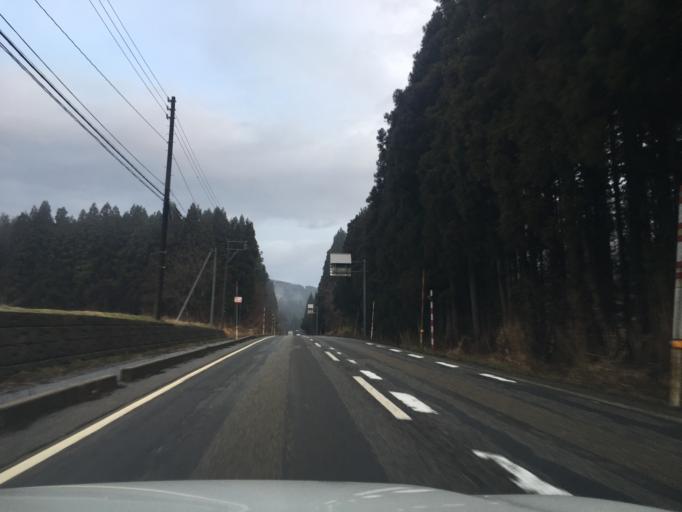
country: JP
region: Niigata
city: Murakami
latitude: 38.3646
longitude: 139.5528
